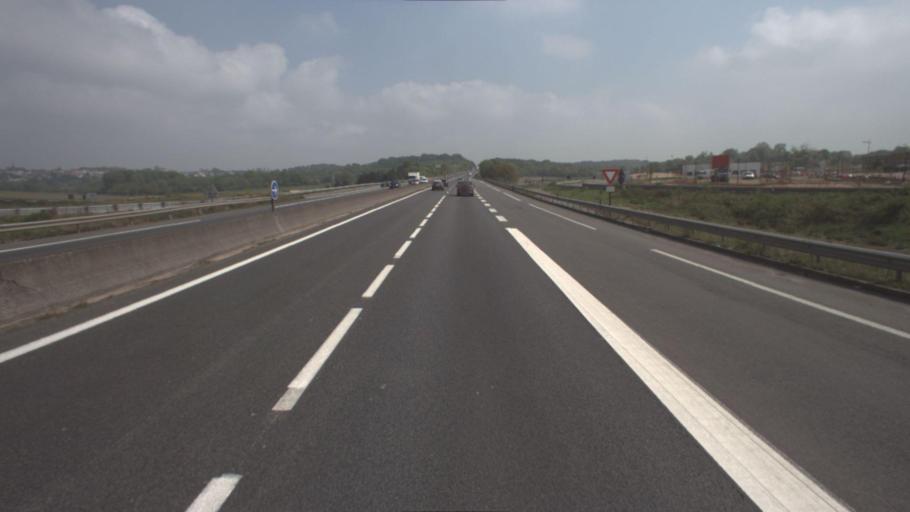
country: FR
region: Ile-de-France
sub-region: Departement de Seine-et-Marne
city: Saint-Mard
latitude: 49.0385
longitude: 2.6818
